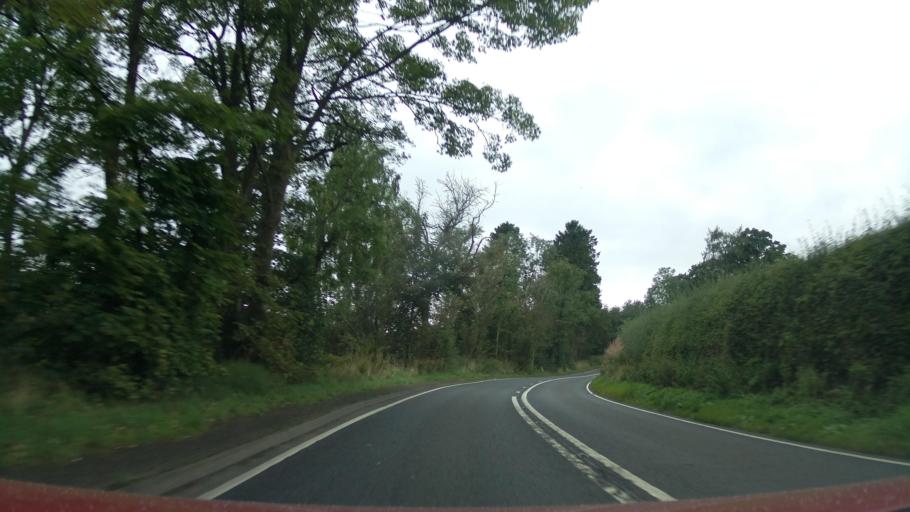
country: GB
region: Scotland
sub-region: Clackmannanshire
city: Tillicoultry
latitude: 56.1554
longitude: -3.7146
